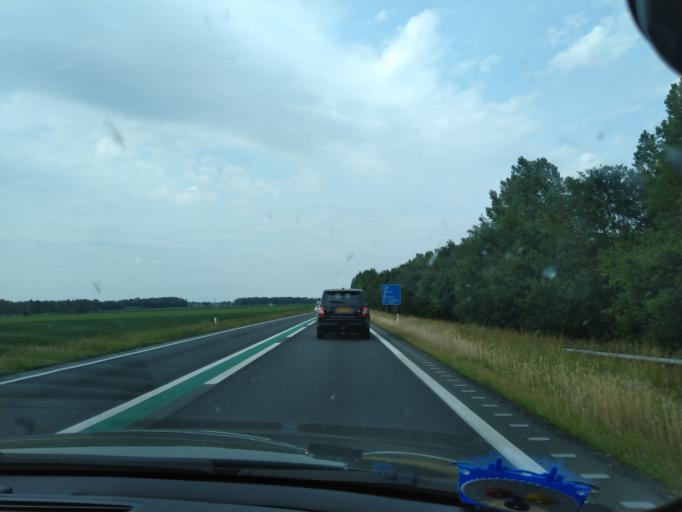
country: NL
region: Drenthe
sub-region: Gemeente Coevorden
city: Dalen
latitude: 52.6978
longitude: 6.7439
